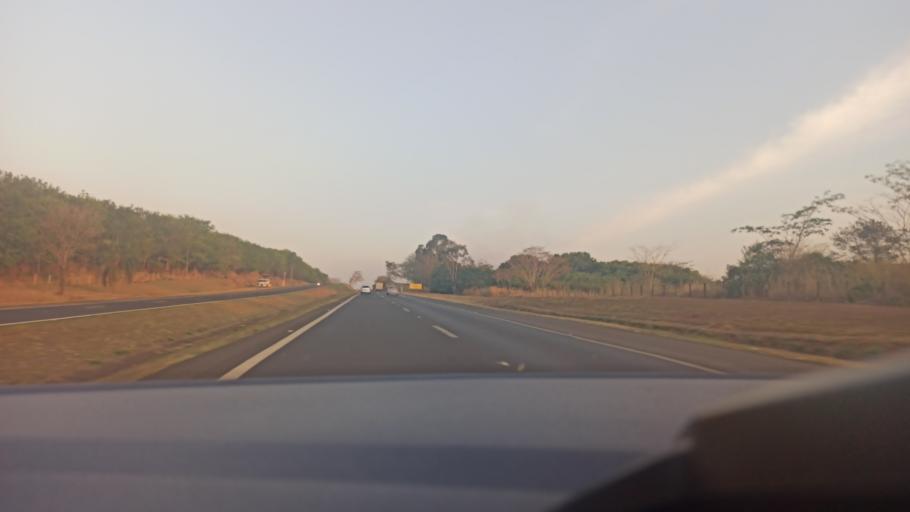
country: BR
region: Sao Paulo
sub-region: Taquaritinga
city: Taquaritinga
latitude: -21.4507
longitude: -48.6347
